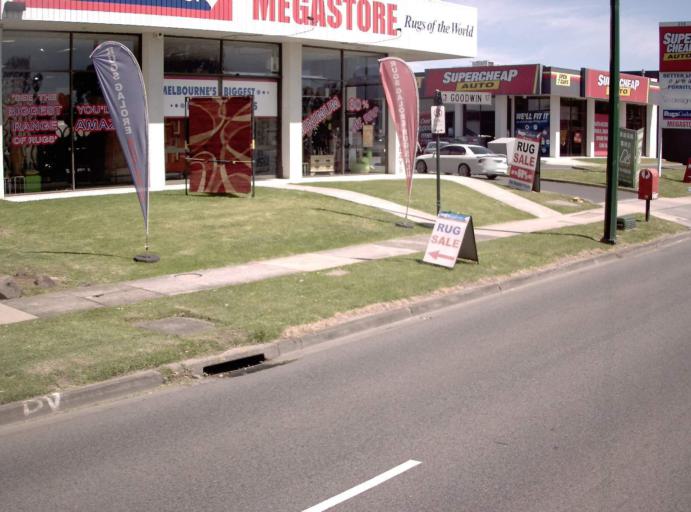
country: AU
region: Victoria
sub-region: Whitehorse
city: Blackburn
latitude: -37.8181
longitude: 145.1633
